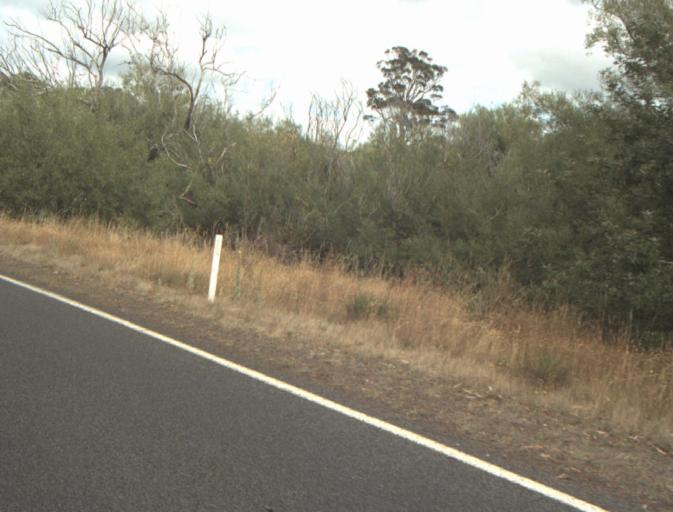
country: AU
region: Tasmania
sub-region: Northern Midlands
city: Evandale
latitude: -41.4766
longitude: 147.5373
